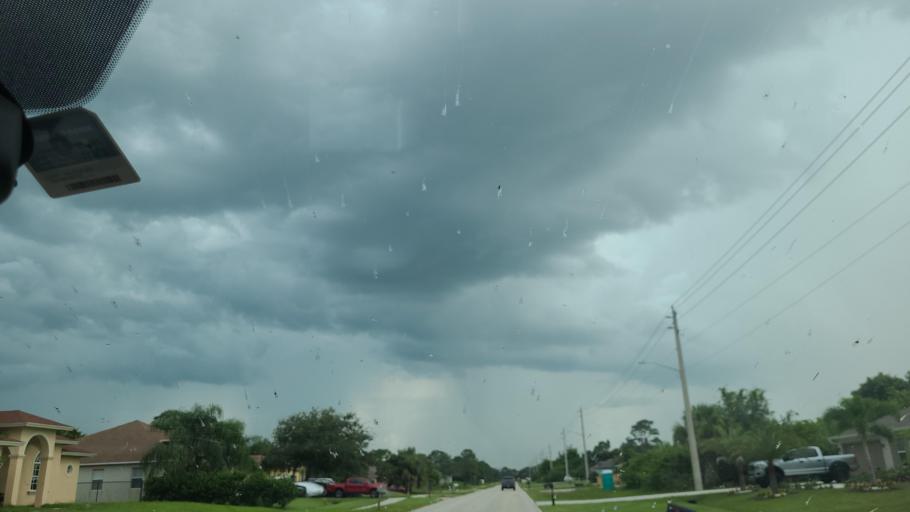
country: US
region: Florida
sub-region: Saint Lucie County
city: Port Saint Lucie
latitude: 27.2155
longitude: -80.3835
